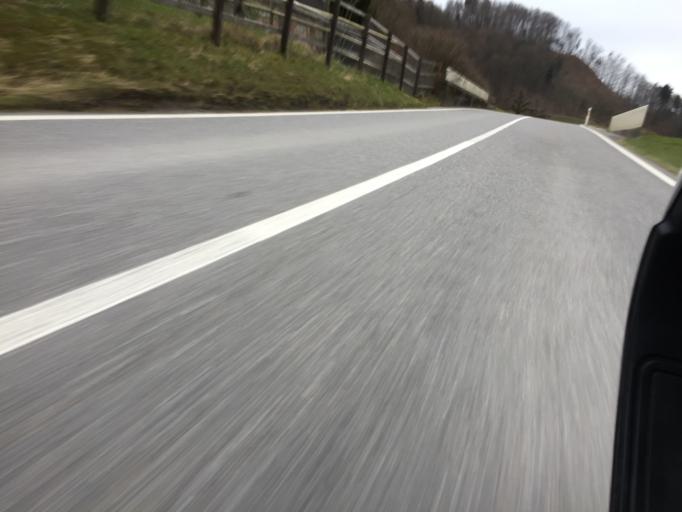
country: CH
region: Bern
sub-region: Emmental District
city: Krauchthal
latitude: 47.0228
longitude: 7.5775
